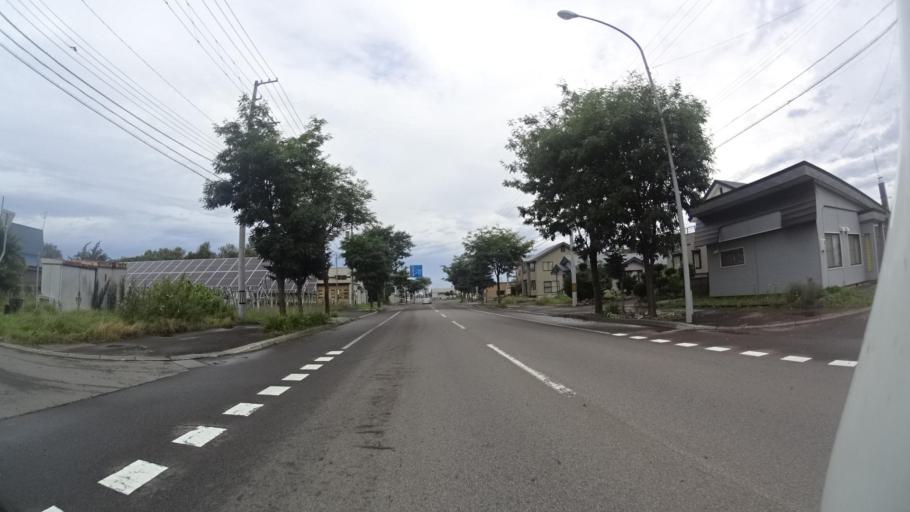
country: JP
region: Hokkaido
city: Abashiri
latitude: 43.8401
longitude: 144.5958
